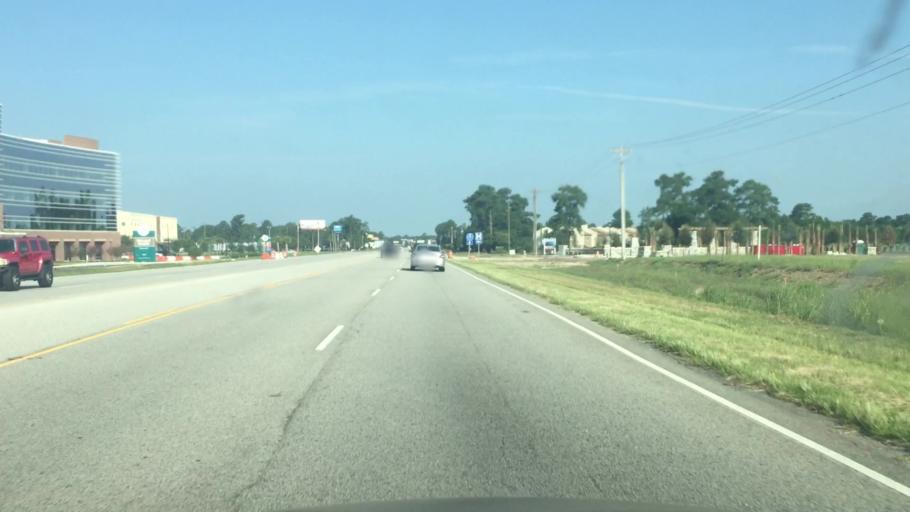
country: US
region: South Carolina
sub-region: Horry County
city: Little River
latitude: 33.8660
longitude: -78.6616
